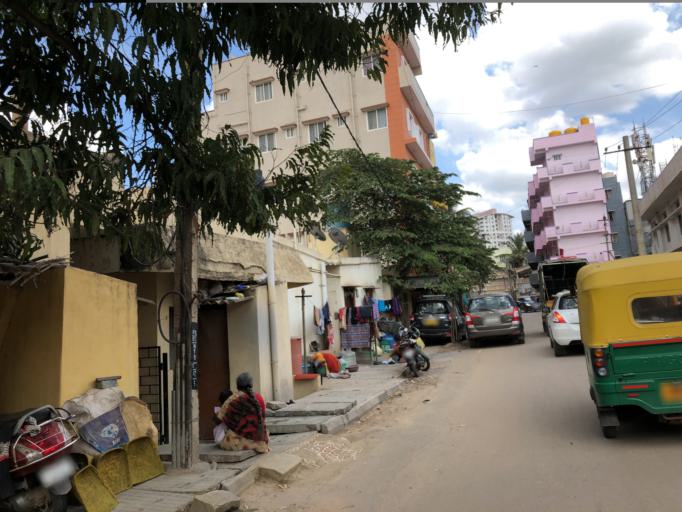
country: IN
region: Karnataka
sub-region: Bangalore Urban
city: Bangalore
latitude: 12.9901
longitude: 77.6970
